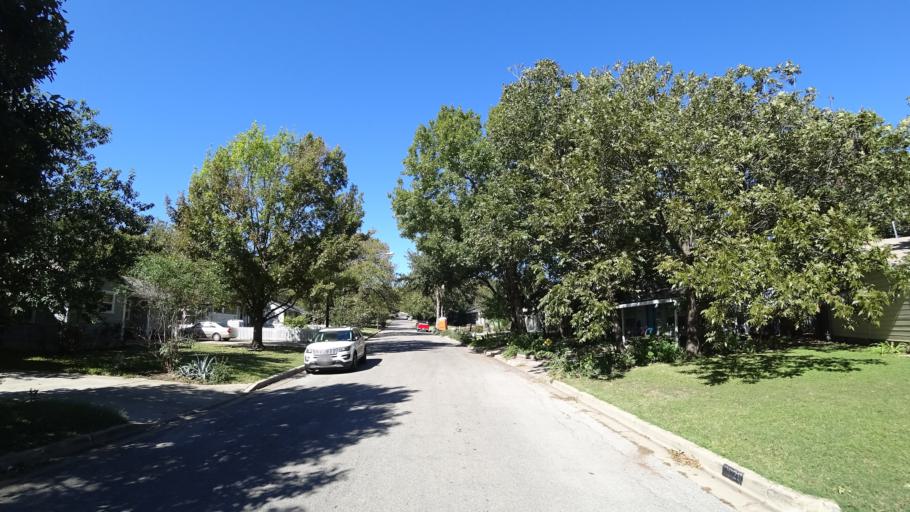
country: US
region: Texas
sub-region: Travis County
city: Austin
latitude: 30.3236
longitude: -97.7482
